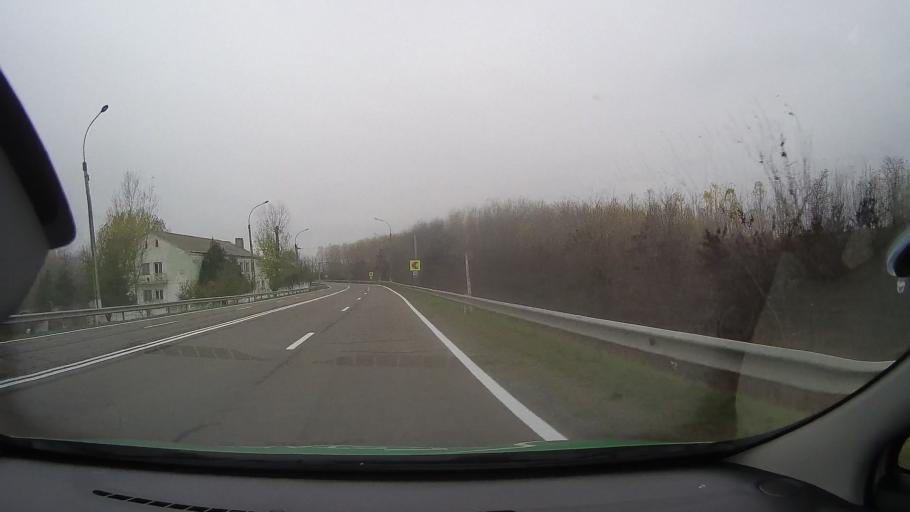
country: RO
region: Ialomita
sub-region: Comuna Giurgeni
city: Giurgeni
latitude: 44.7559
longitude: 27.8660
